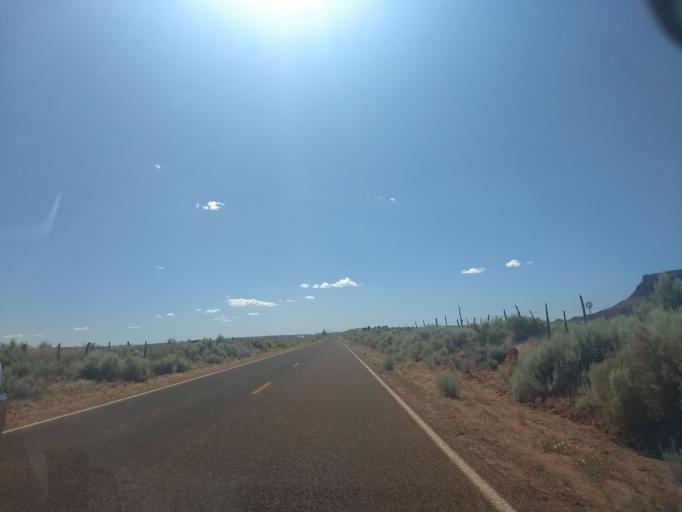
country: US
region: Arizona
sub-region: Mohave County
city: Colorado City
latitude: 36.9470
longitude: -112.9097
